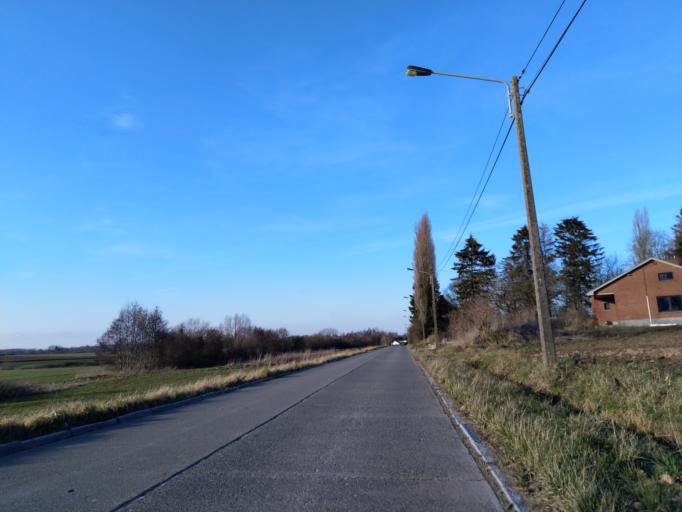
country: BE
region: Wallonia
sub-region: Province du Hainaut
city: Quevy-le-Petit
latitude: 50.3463
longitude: 3.8993
